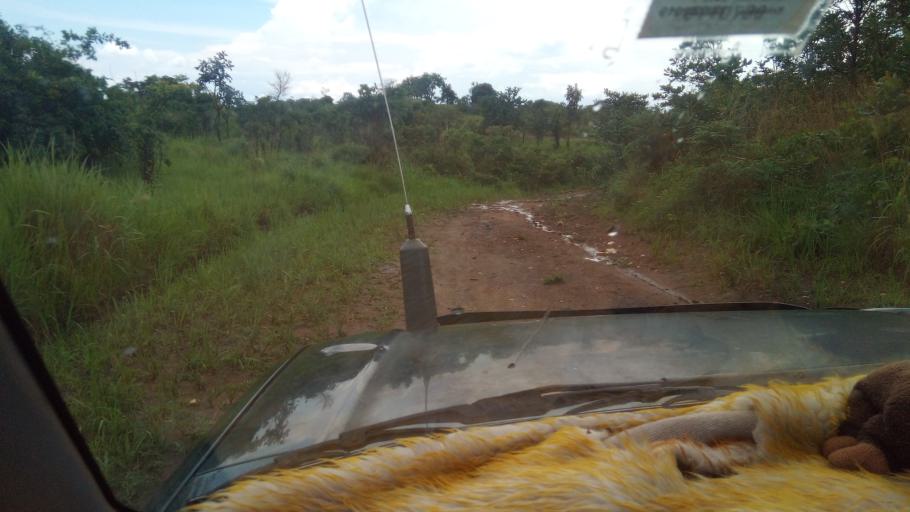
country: CD
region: Katanga
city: Kalemie
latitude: -5.7109
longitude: 29.3013
